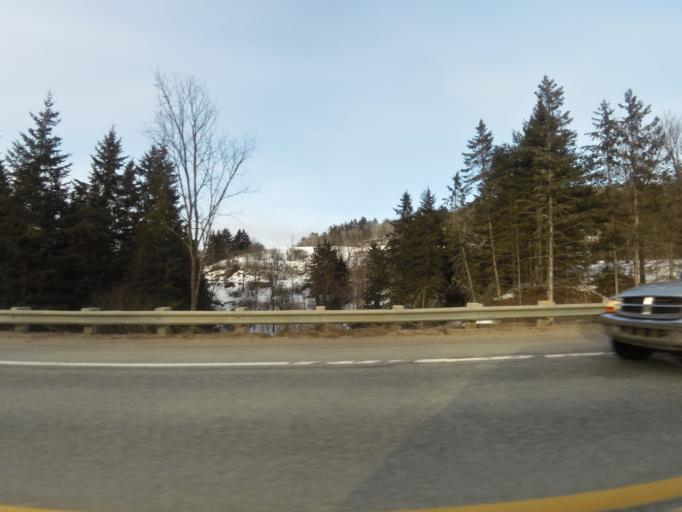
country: CA
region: Quebec
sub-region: Outaouais
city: Wakefield
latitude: 45.8483
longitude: -75.9889
